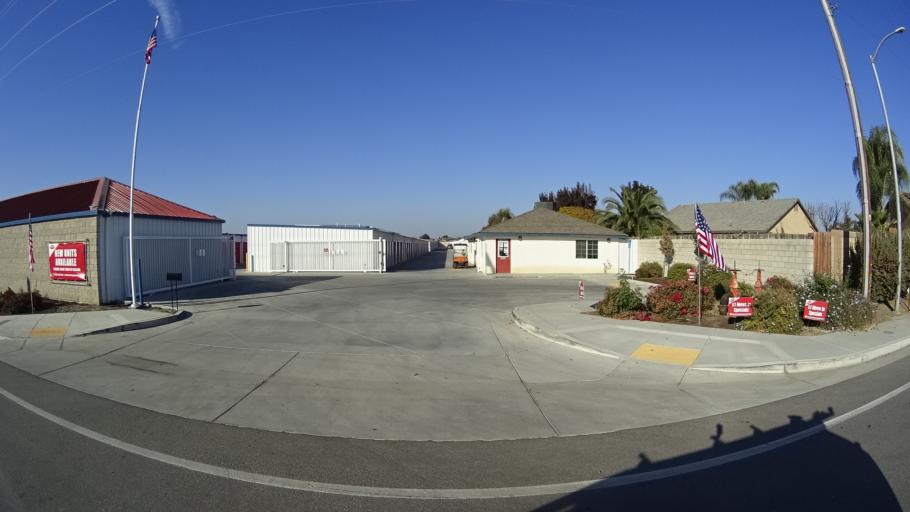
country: US
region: California
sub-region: Kern County
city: Greenacres
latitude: 35.2962
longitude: -119.1055
